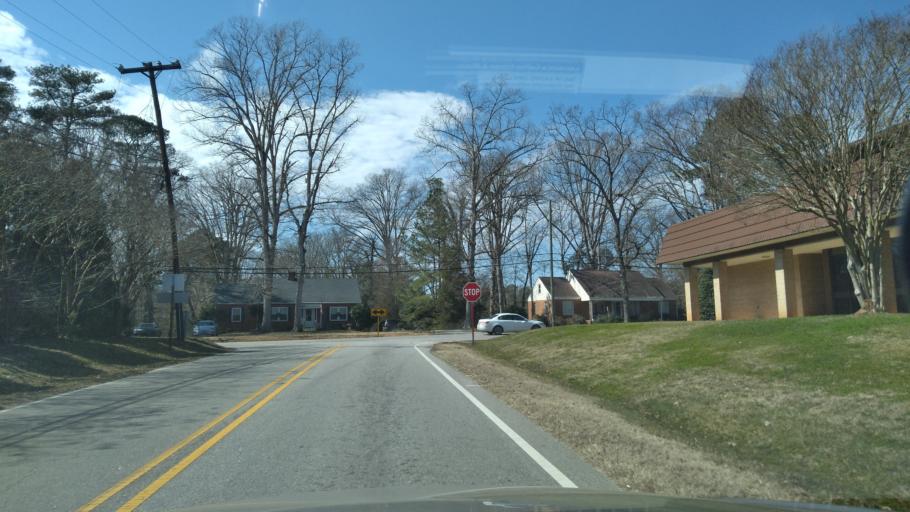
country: US
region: North Carolina
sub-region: Wake County
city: Garner
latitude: 35.7098
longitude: -78.6563
